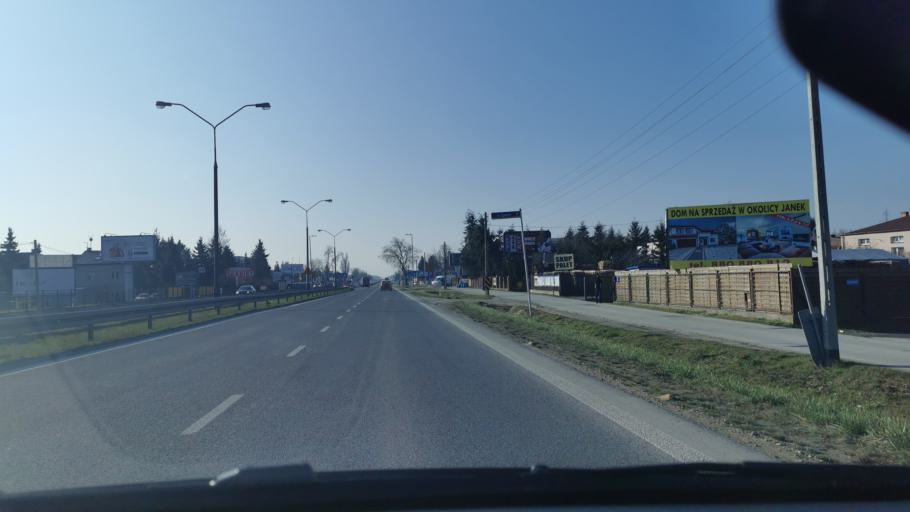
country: PL
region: Masovian Voivodeship
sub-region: Powiat pruszkowski
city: Nowe Grocholice
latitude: 52.1263
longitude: 20.8955
